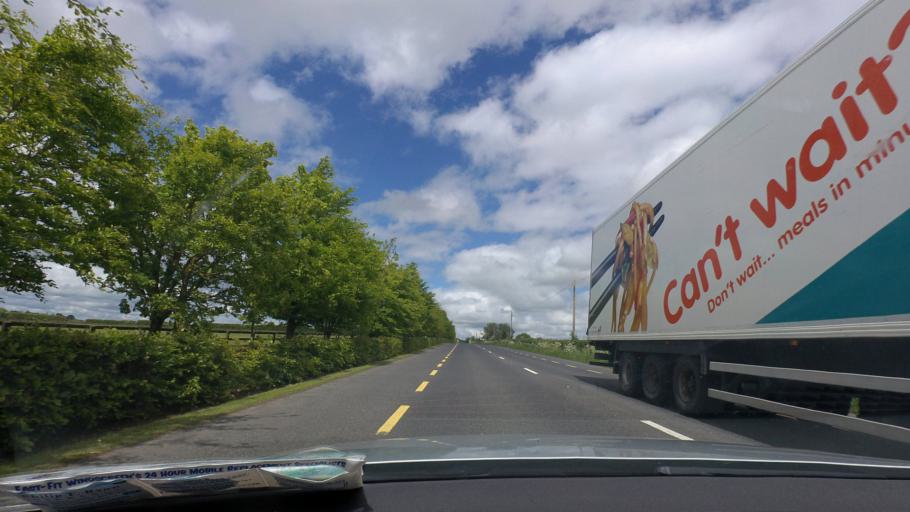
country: IE
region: Munster
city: Cashel
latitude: 52.5668
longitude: -7.8436
